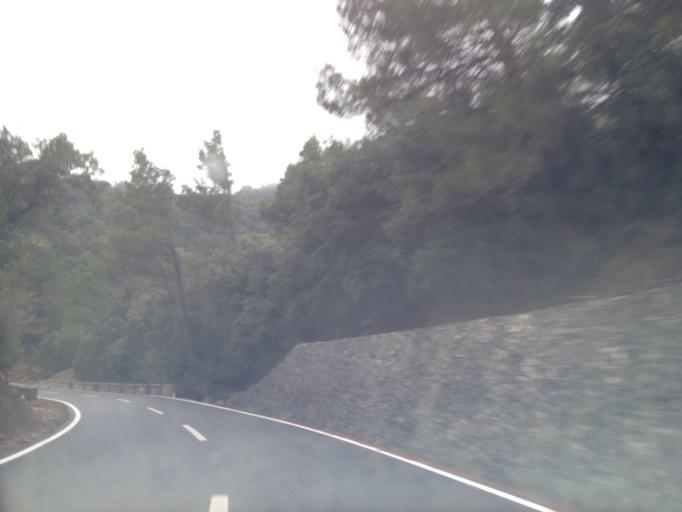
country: ES
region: Balearic Islands
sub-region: Illes Balears
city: Fornalutx
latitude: 39.7950
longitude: 2.7715
